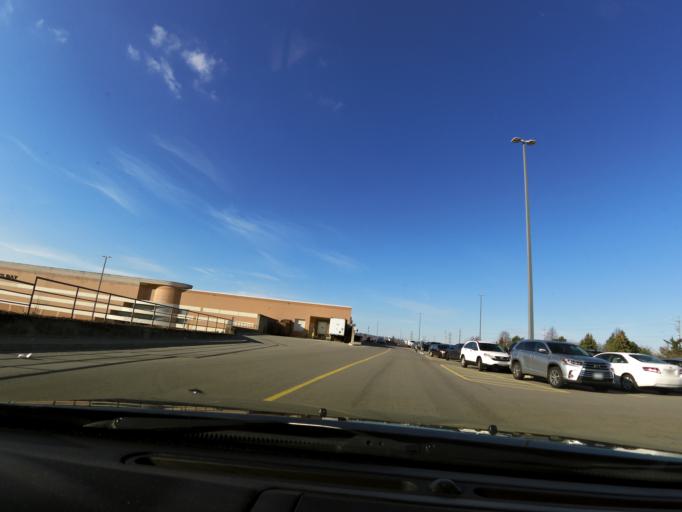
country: CA
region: Ontario
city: Burlington
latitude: 43.3238
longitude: -79.8175
